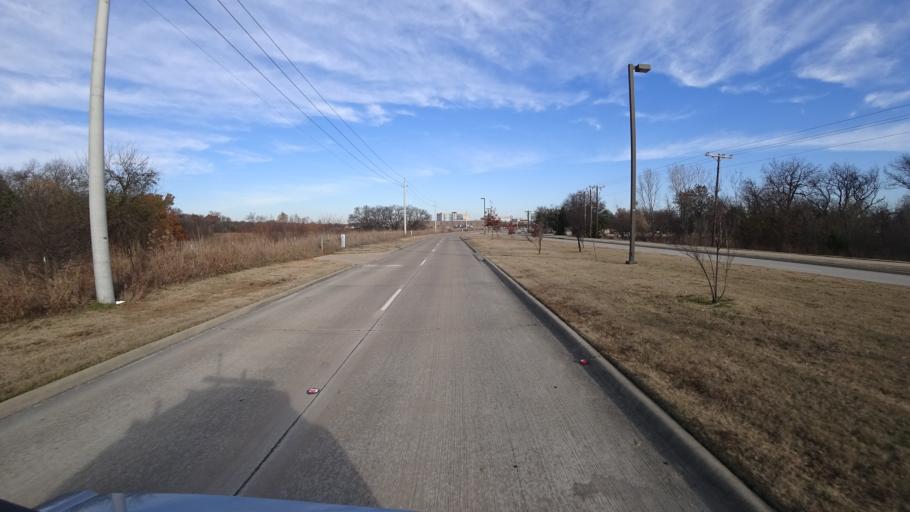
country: US
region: Texas
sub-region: Collin County
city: McKinney
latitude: 33.2117
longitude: -96.6798
